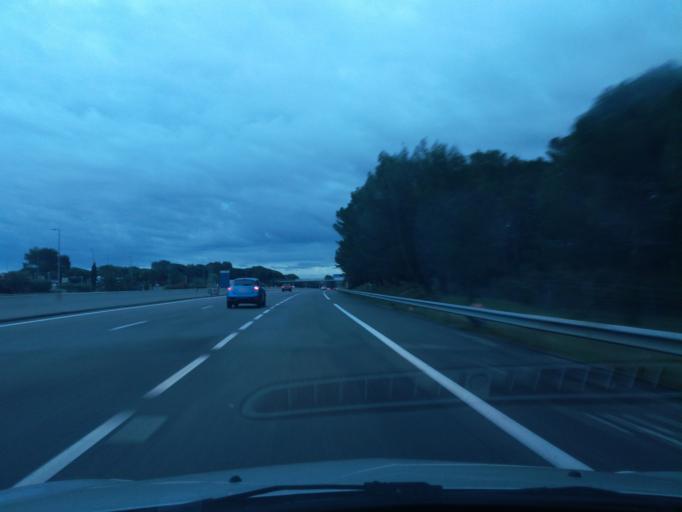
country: FR
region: Provence-Alpes-Cote d'Azur
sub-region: Departement du Var
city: Puget-sur-Argens
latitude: 43.4664
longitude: 6.6706
